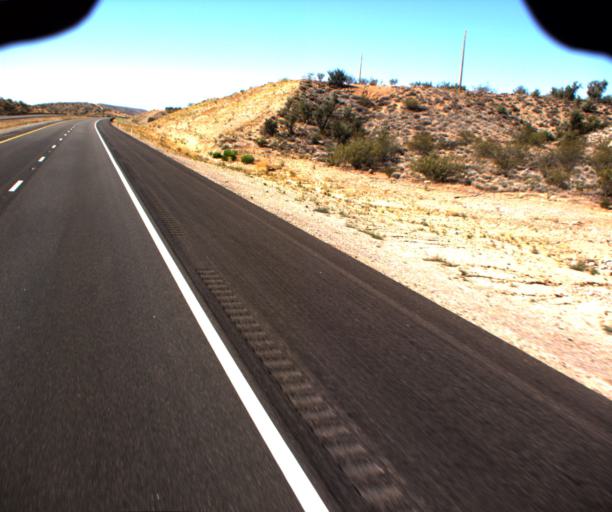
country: US
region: Arizona
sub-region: Mohave County
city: Kingman
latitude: 35.0171
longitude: -113.6646
